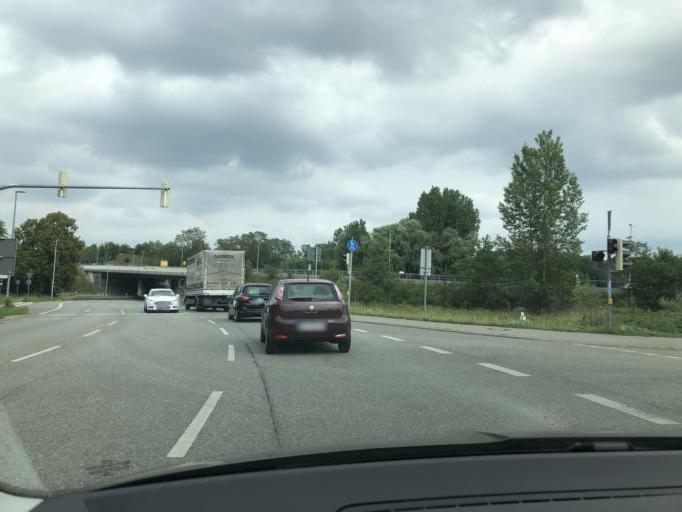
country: DE
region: Mecklenburg-Vorpommern
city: Neumuehle
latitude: 53.6246
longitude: 11.3611
